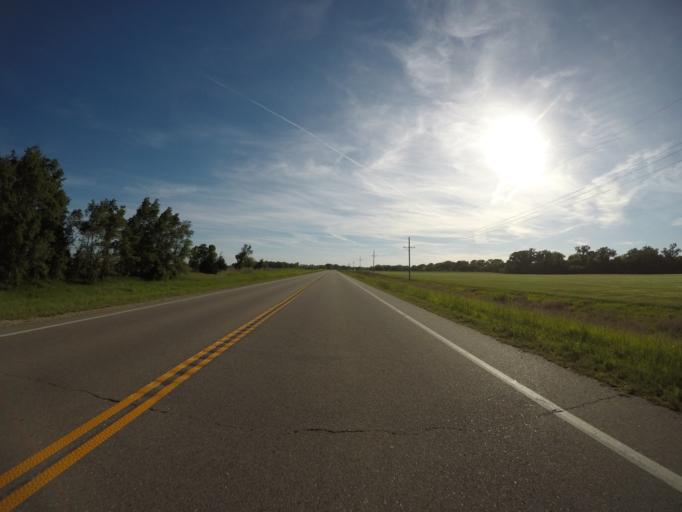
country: US
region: Kansas
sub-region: Cloud County
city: Concordia
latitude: 39.5746
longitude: -97.4254
